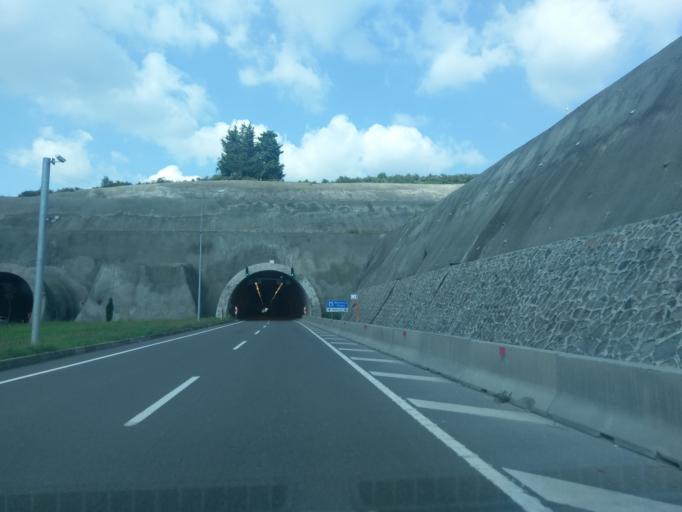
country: TR
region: Ordu
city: Unieh
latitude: 41.1138
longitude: 37.2880
